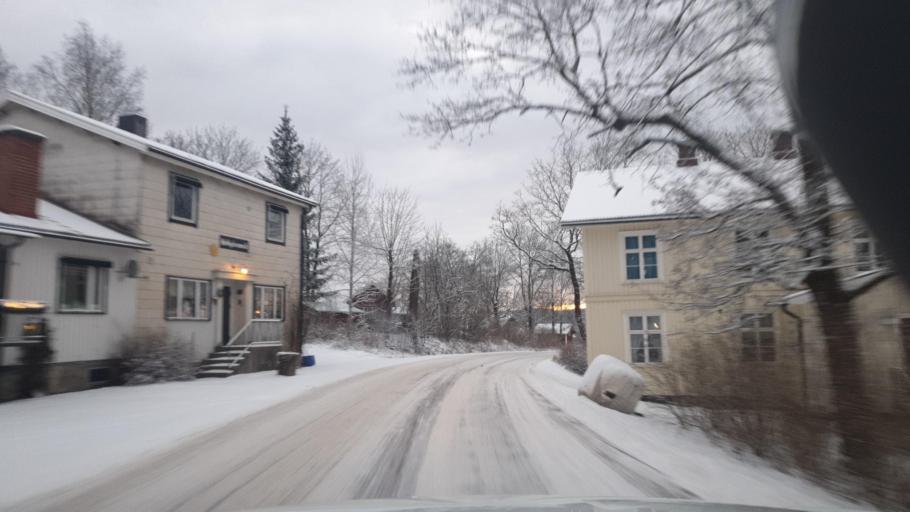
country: SE
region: Vaermland
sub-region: Eda Kommun
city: Charlottenberg
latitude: 59.7475
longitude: 12.1628
